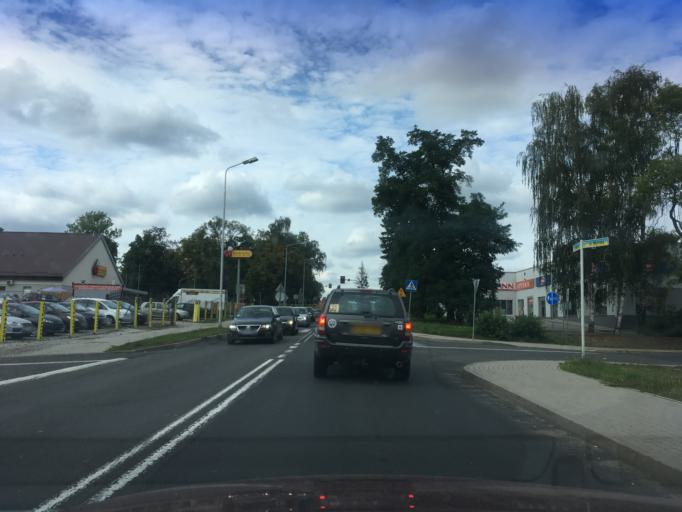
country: PL
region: Lower Silesian Voivodeship
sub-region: Powiat lwowecki
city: Gryfow Slaski
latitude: 51.0309
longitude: 15.4213
